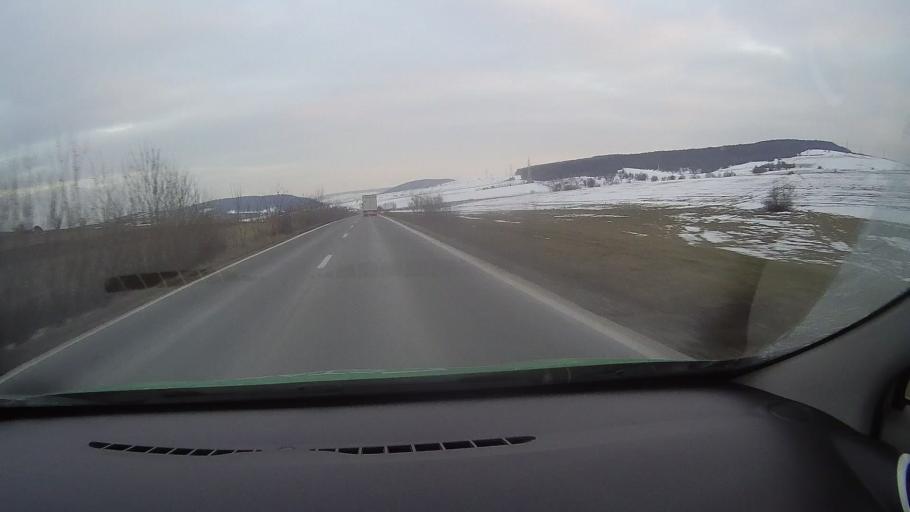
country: RO
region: Harghita
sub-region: Comuna Lupeni
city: Lupeni
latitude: 46.3571
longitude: 25.2514
